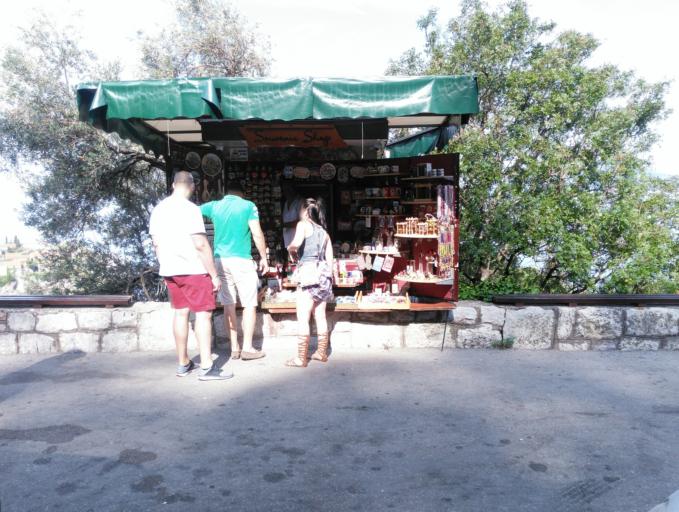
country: ME
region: Budva
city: Budva
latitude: 42.2580
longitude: 18.8960
